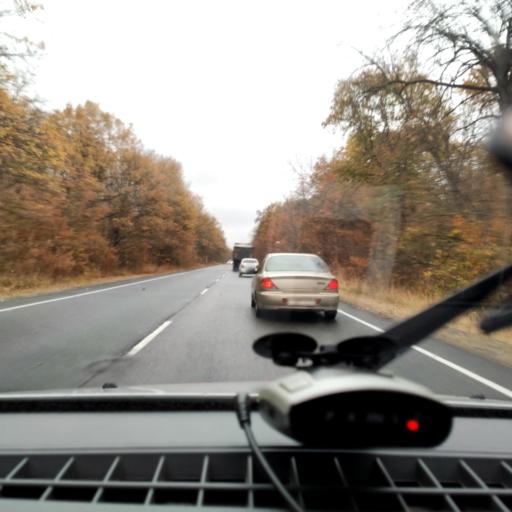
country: RU
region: Voronezj
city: Devitsa
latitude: 51.6225
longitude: 38.9872
